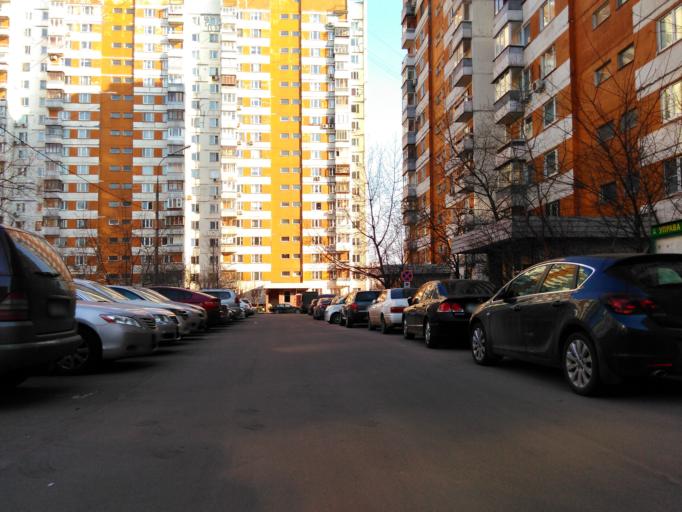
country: RU
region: Moscow
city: Ramenki
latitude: 55.6956
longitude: 37.5029
